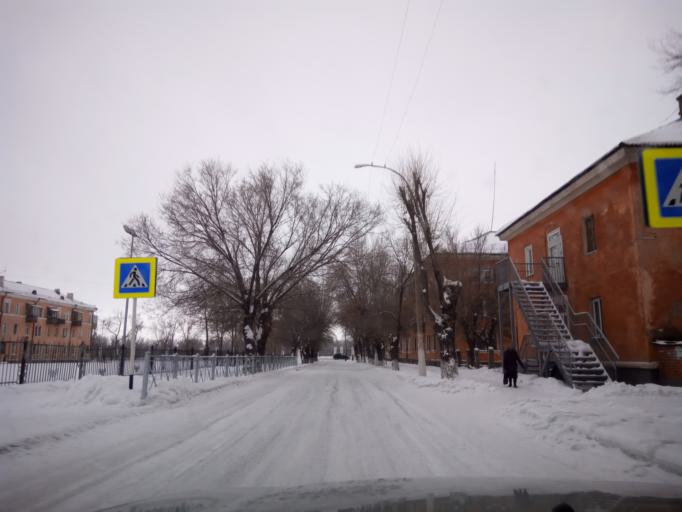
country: RU
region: Orenburg
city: Novotroitsk
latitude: 51.1969
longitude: 58.3270
